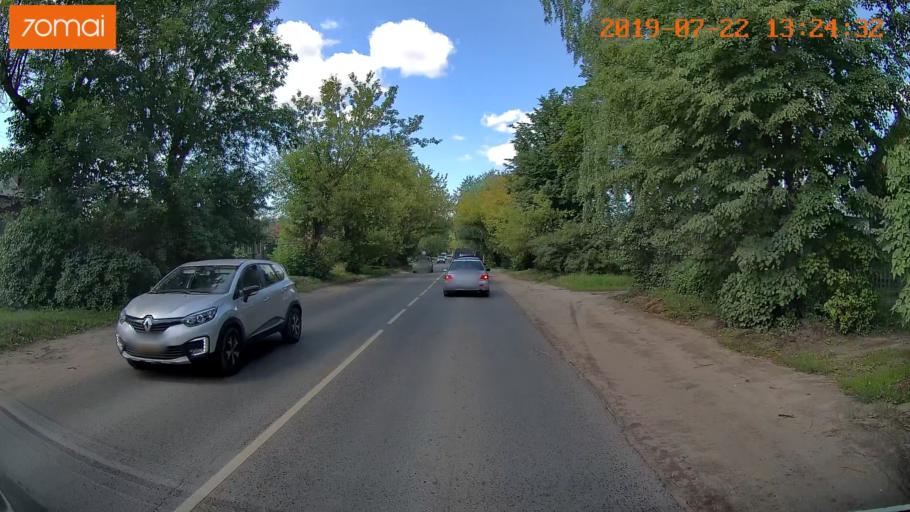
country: RU
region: Ivanovo
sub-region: Gorod Ivanovo
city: Ivanovo
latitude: 57.0267
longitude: 40.9514
